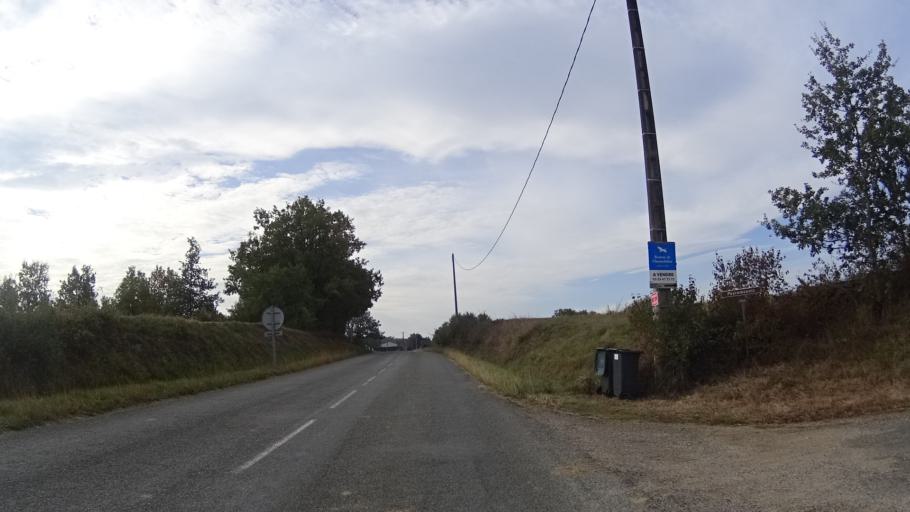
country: FR
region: Aquitaine
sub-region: Departement du Lot-et-Garonne
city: Boe
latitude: 44.1266
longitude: 0.5977
